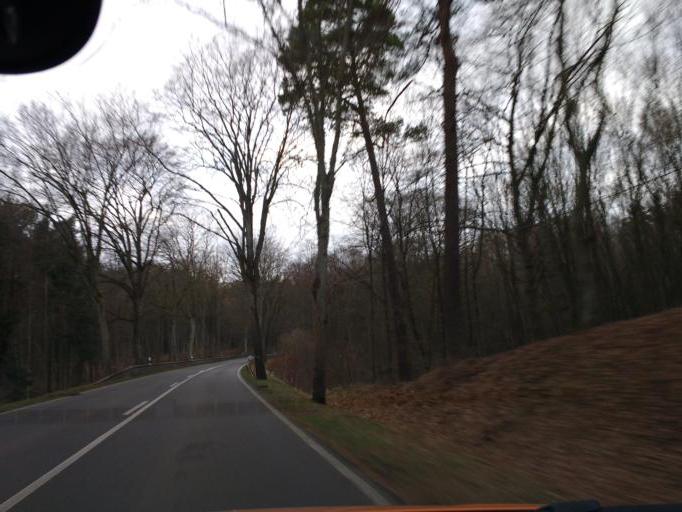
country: DE
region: Brandenburg
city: Strausberg
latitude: 52.6489
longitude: 13.9081
